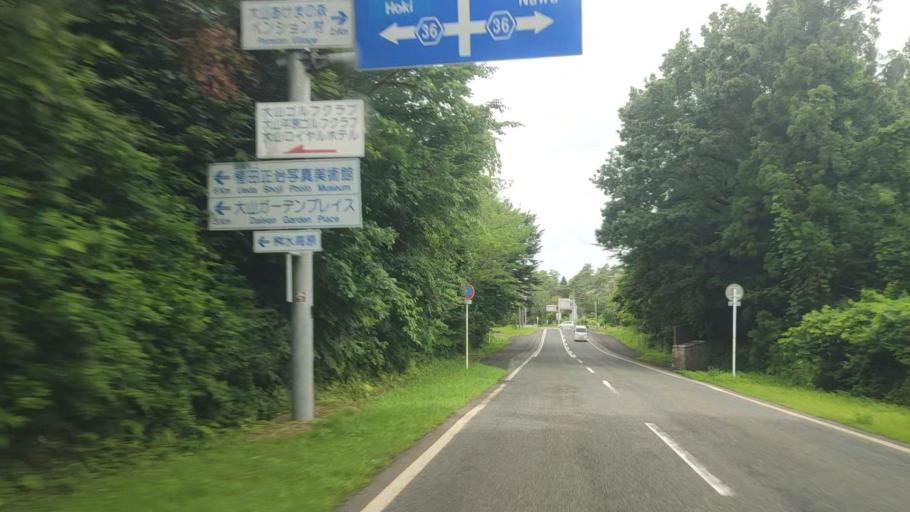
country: JP
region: Tottori
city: Yonago
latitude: 35.4073
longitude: 133.4809
